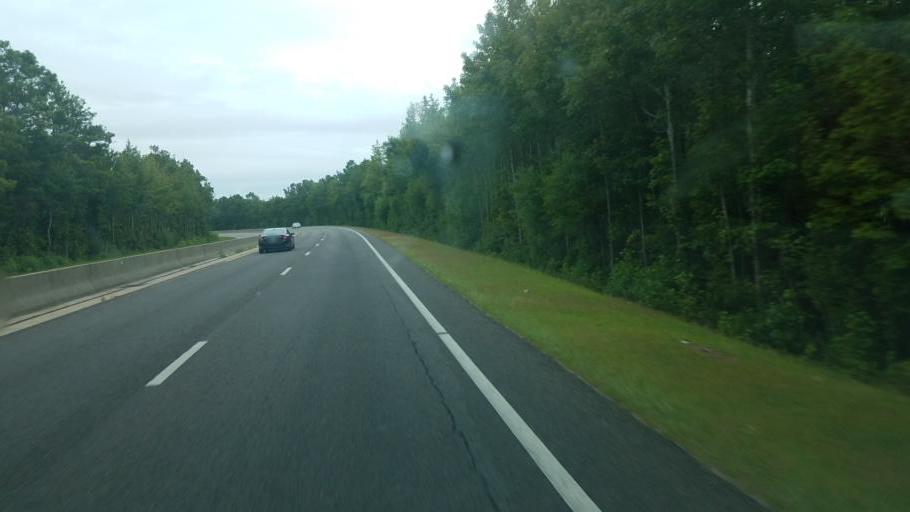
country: US
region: North Carolina
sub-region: Currituck County
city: Currituck
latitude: 36.3483
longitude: -75.9595
